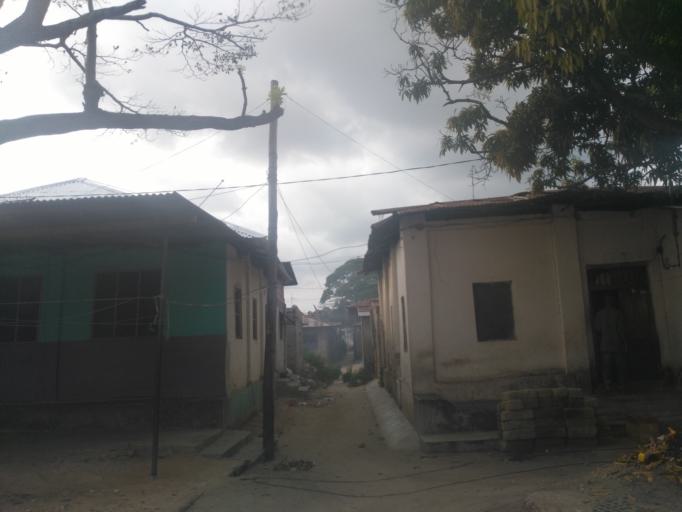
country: TZ
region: Zanzibar Urban/West
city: Zanzibar
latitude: -6.1689
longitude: 39.2007
